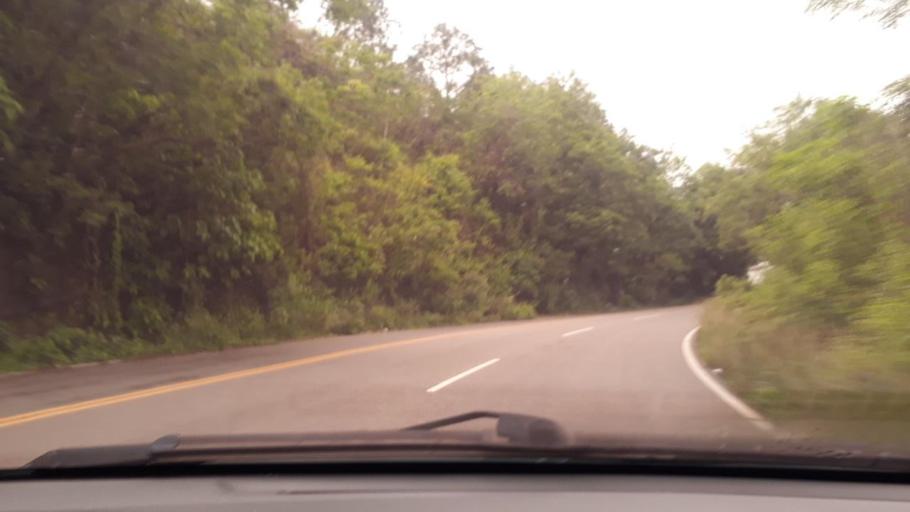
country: GT
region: Chiquimula
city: Esquipulas
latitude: 14.5615
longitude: -89.3646
